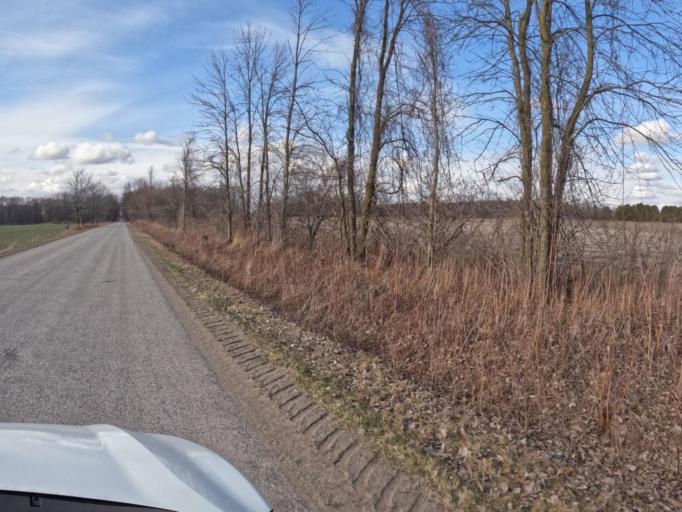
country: CA
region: Ontario
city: Brant
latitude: 42.9946
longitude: -80.4099
